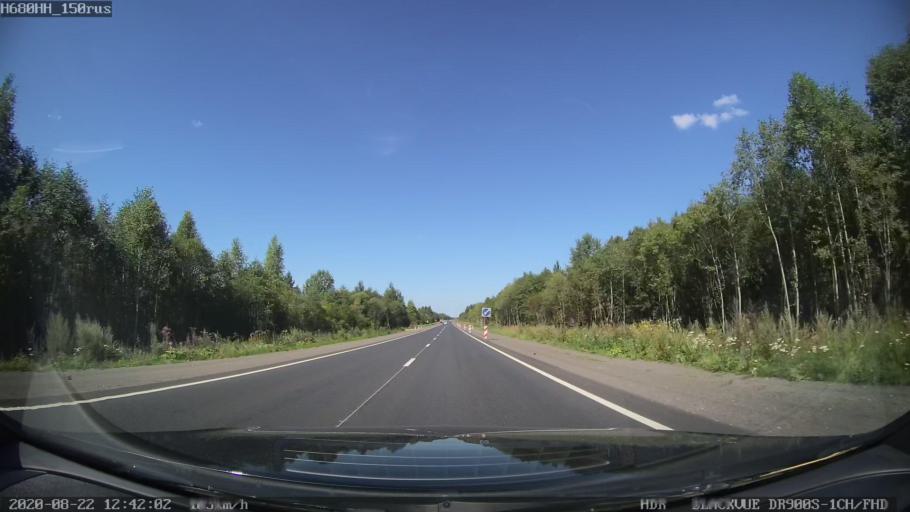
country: RU
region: Tverskaya
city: Rameshki
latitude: 57.3557
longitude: 36.0971
